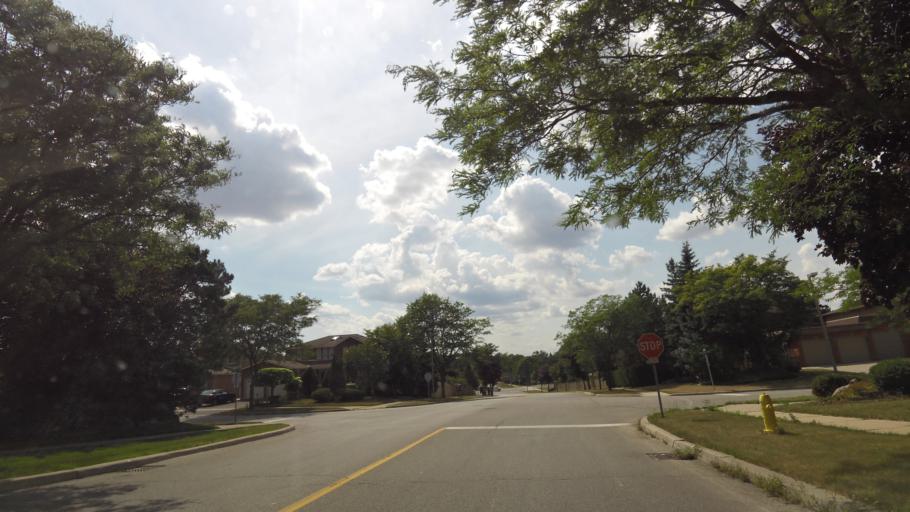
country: CA
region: Ontario
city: Vaughan
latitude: 43.7888
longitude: -79.5717
